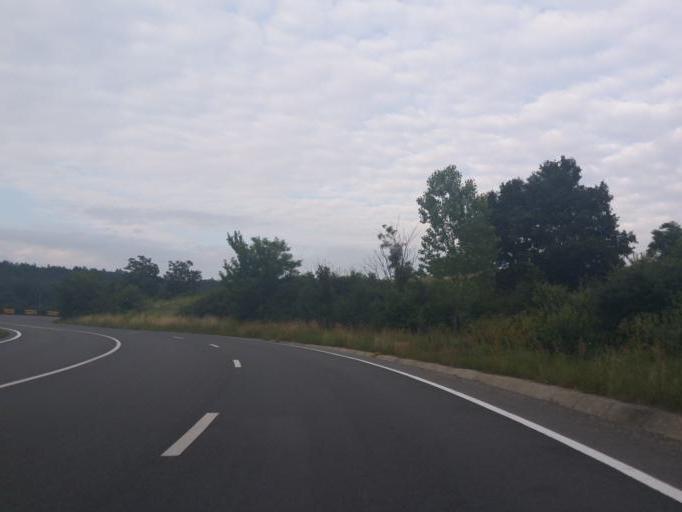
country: RO
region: Cluj
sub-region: Comuna Sanpaul
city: Sanpaul
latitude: 46.9448
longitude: 23.3811
